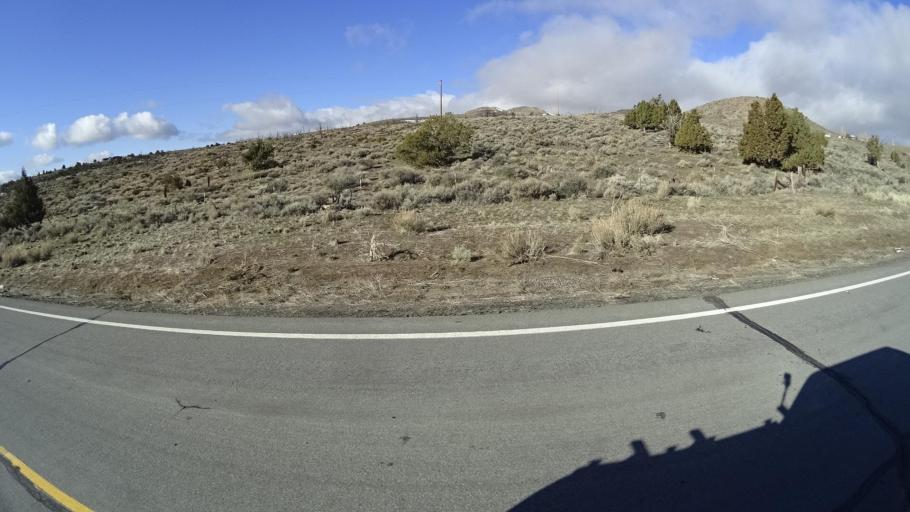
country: US
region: Nevada
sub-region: Washoe County
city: Cold Springs
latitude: 39.7774
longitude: -119.8942
